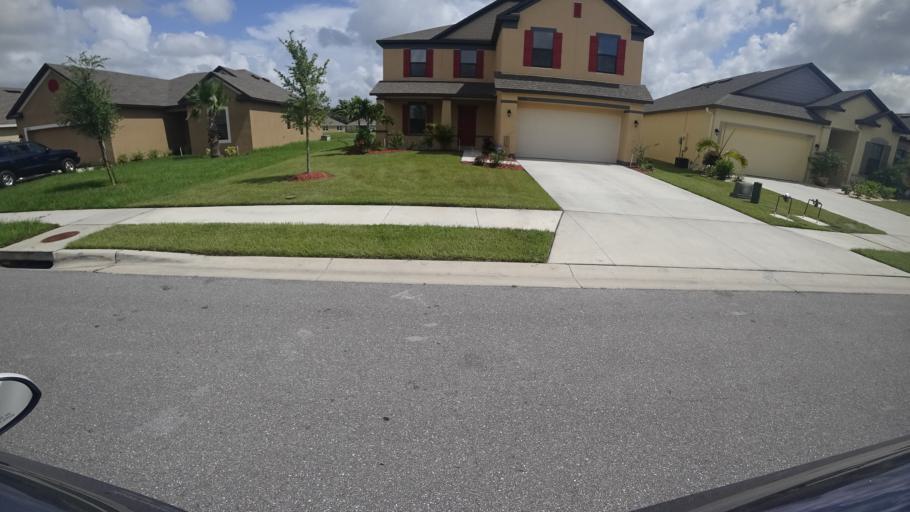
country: US
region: Florida
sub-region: Manatee County
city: Ellenton
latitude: 27.5493
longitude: -82.5193
